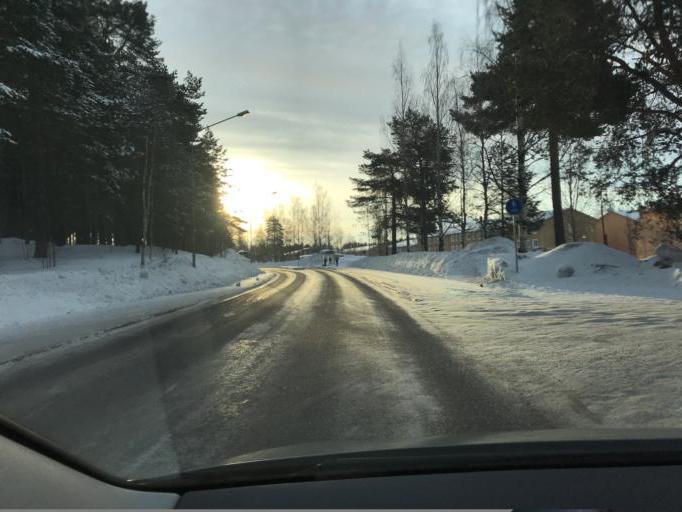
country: SE
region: Norrbotten
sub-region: Lulea Kommun
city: Bergnaset
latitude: 65.6097
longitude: 22.1013
